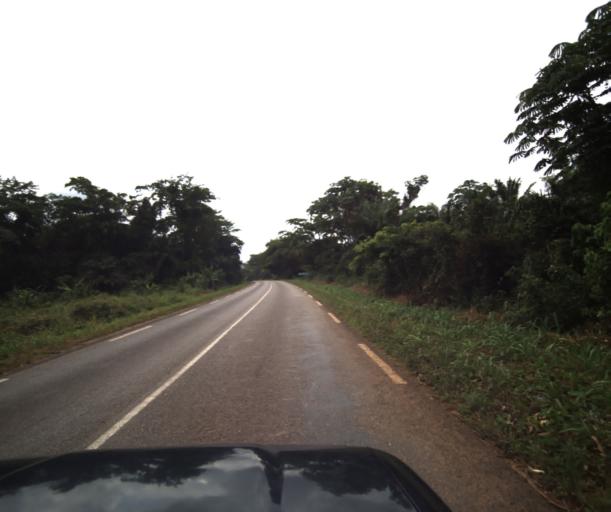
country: CM
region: Centre
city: Eseka
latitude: 3.8502
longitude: 10.4909
